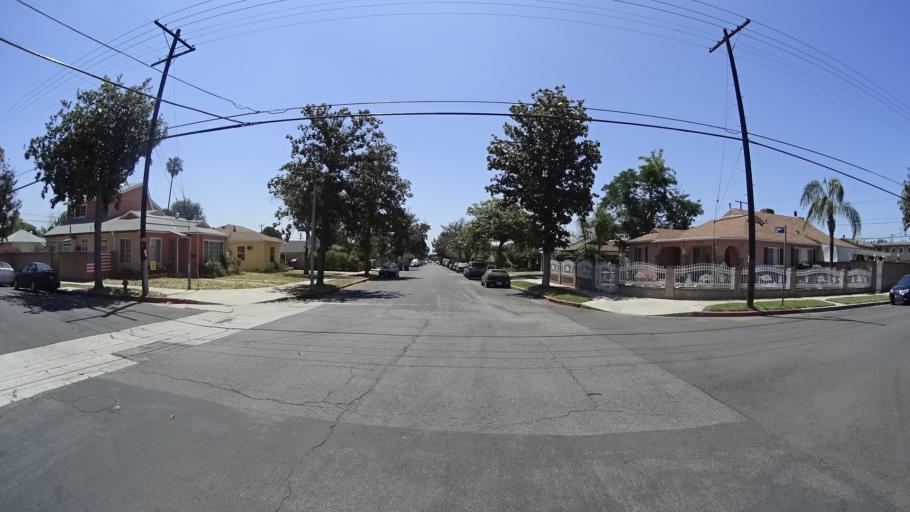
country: US
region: California
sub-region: Los Angeles County
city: Van Nuys
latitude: 34.2304
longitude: -118.4351
